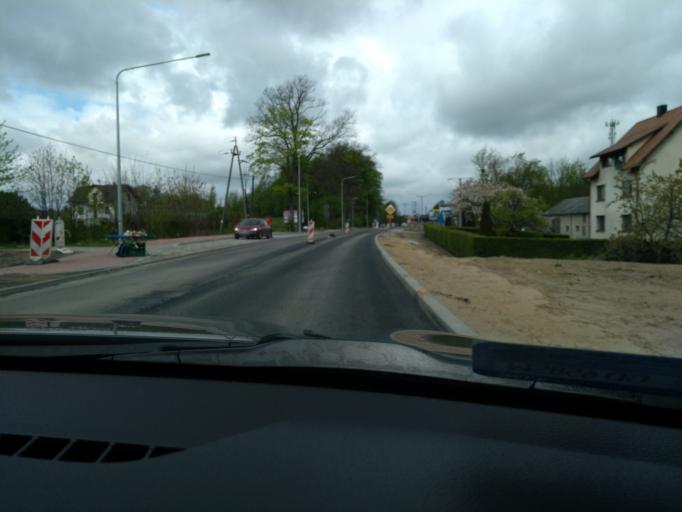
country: PL
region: Pomeranian Voivodeship
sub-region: Powiat kartuski
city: Kartuzy
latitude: 54.3438
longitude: 18.1591
